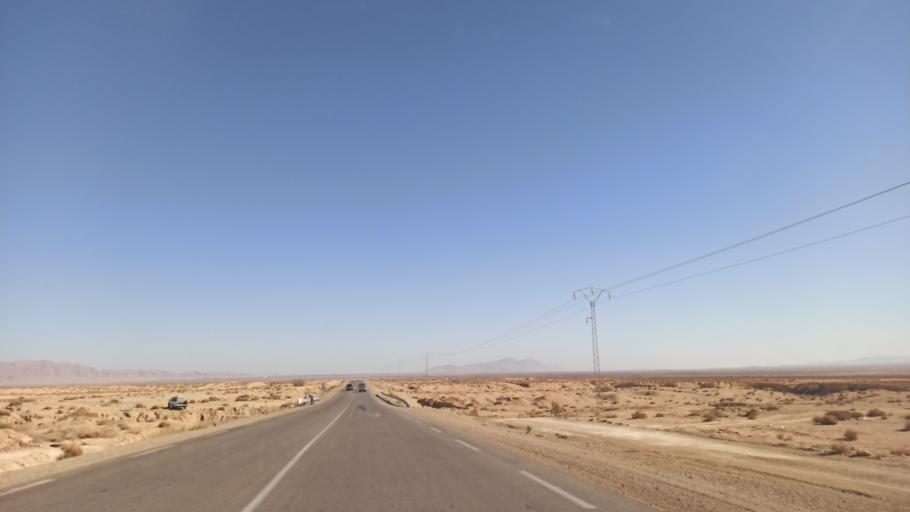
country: TN
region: Gafsa
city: Al Metlaoui
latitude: 34.3256
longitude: 8.5372
